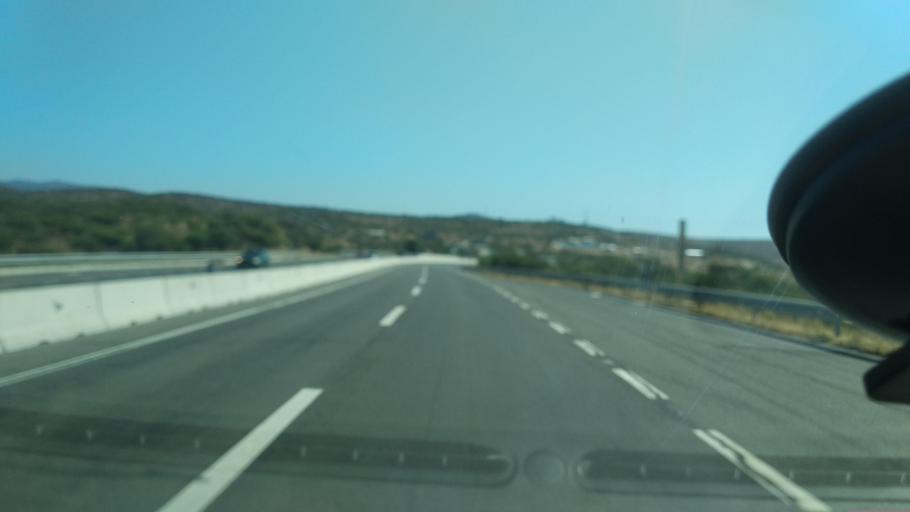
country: CL
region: Valparaiso
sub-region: Provincia de Marga Marga
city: Limache
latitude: -32.9838
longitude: -71.3179
